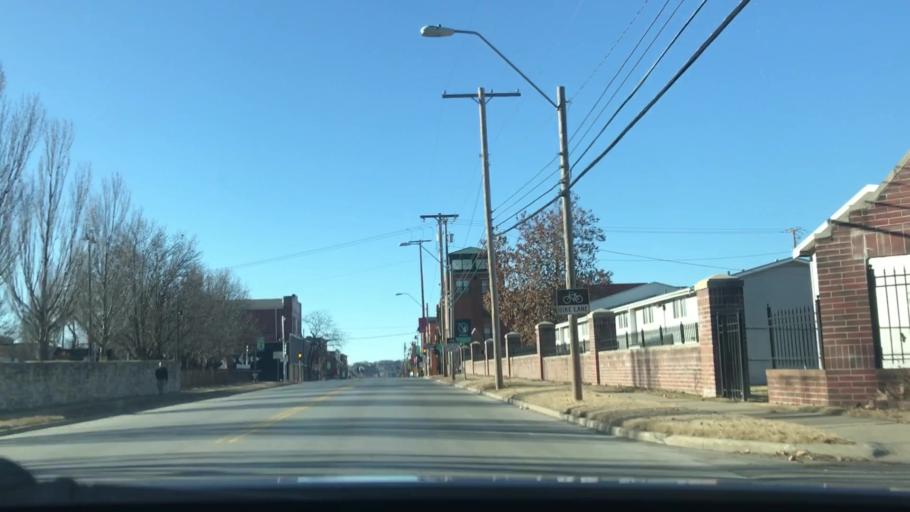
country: US
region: Missouri
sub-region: Jackson County
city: Kansas City
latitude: 39.0911
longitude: -94.5600
